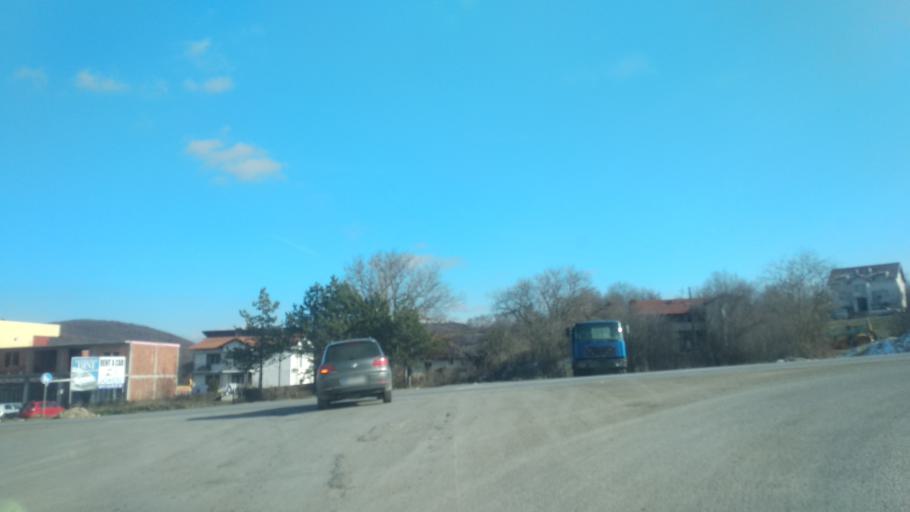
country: XK
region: Pristina
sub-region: Komuna e Prishtines
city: Pristina
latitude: 42.7466
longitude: 21.1402
